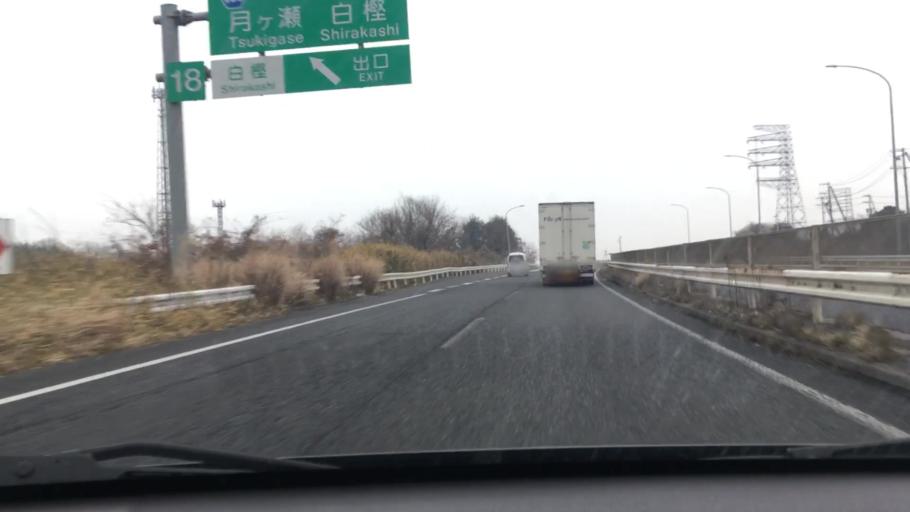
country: JP
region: Mie
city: Ueno-ebisumachi
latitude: 34.7213
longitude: 136.0832
